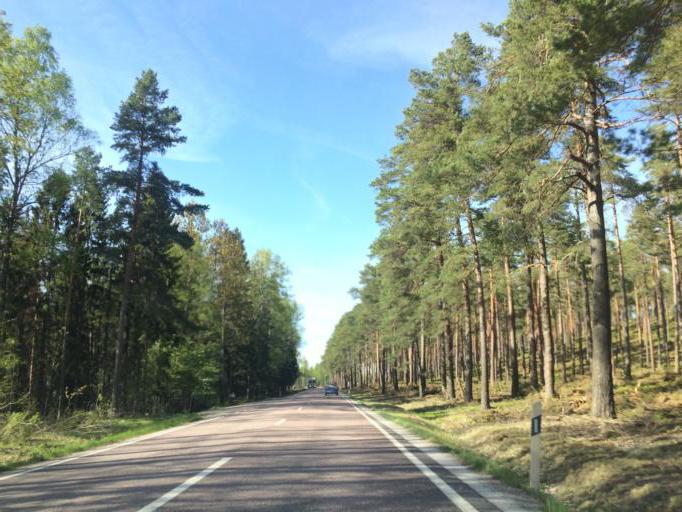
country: SE
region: Vaestmanland
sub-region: Kungsors Kommun
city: Kungsoer
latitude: 59.3900
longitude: 16.1100
